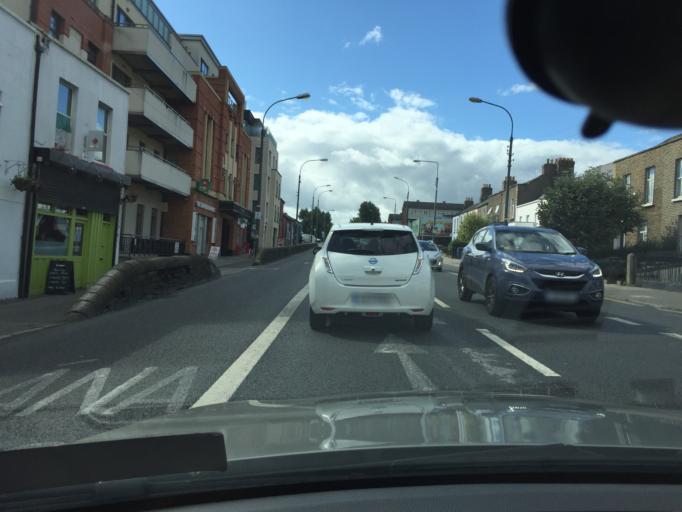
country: IE
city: Fairview
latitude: 53.3575
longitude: -6.2428
